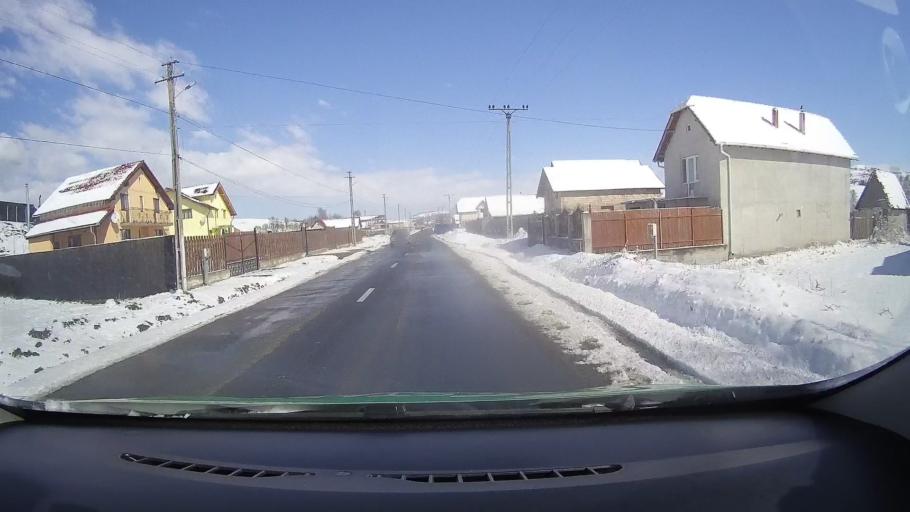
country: RO
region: Sibiu
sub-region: Comuna Vurpar
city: Vurpar
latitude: 45.8868
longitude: 24.3316
